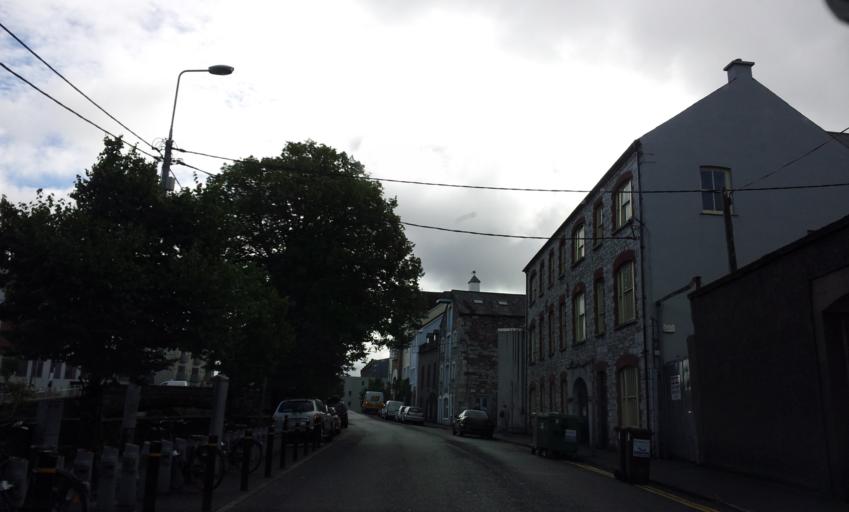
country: IE
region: Munster
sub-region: County Cork
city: Cork
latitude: 51.8964
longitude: -8.4804
